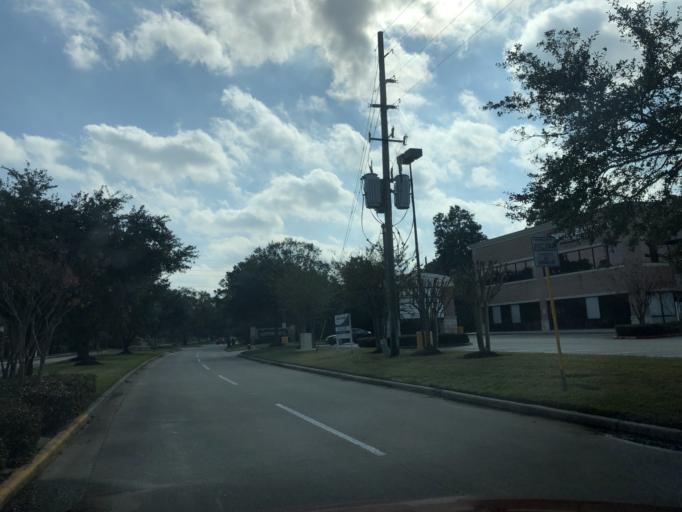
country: US
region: Texas
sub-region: Harris County
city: Tomball
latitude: 30.0318
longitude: -95.5541
